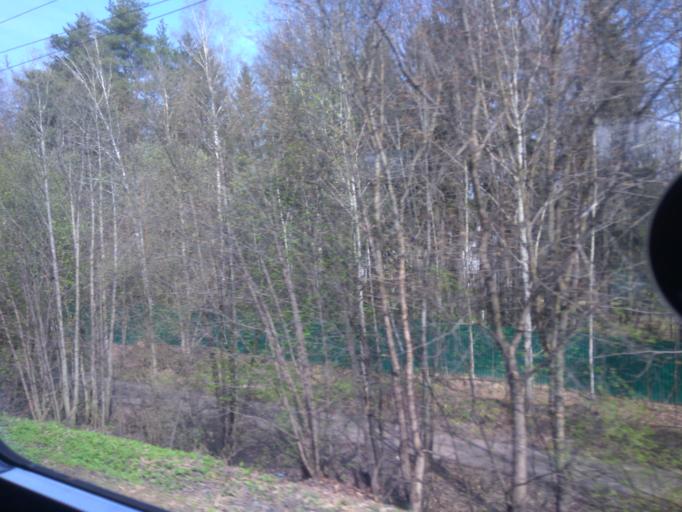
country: RU
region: Moskovskaya
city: Yermolino
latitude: 56.1361
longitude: 37.5140
